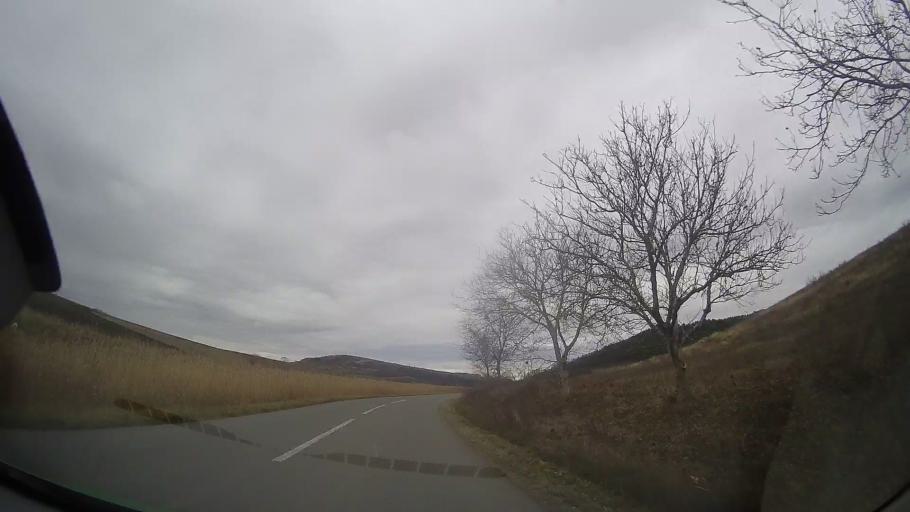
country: RO
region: Mures
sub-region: Comuna Bala
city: Bala
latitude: 46.7190
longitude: 24.5496
